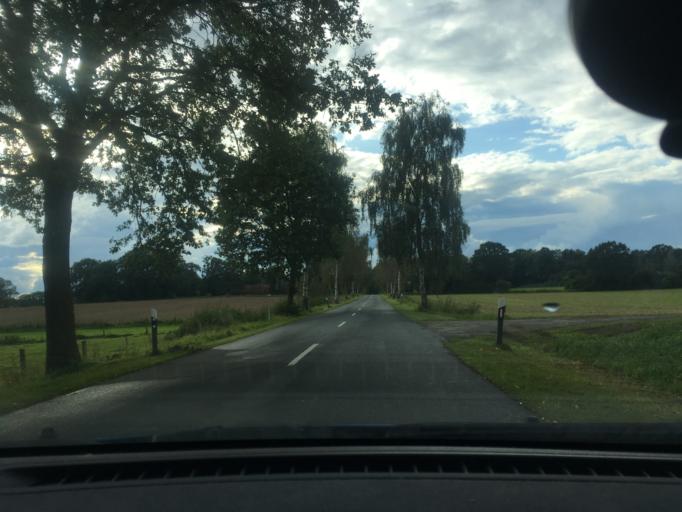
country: DE
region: Lower Saxony
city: Gohrde
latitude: 53.1660
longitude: 10.8587
